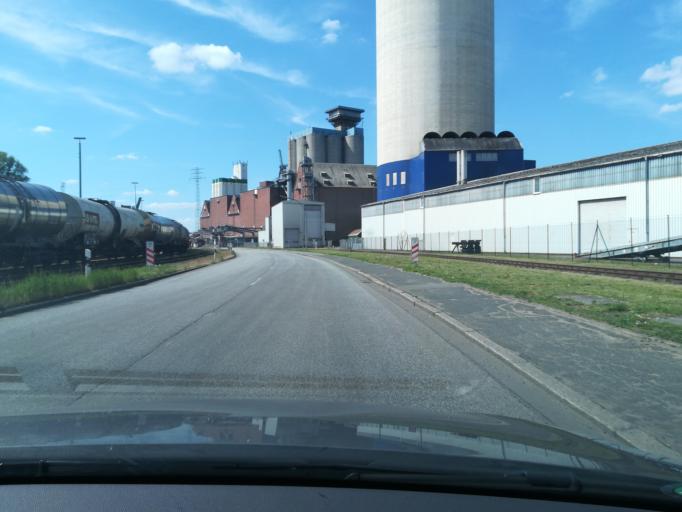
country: DE
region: Hamburg
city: Kleiner Grasbrook
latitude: 53.5003
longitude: 9.9736
